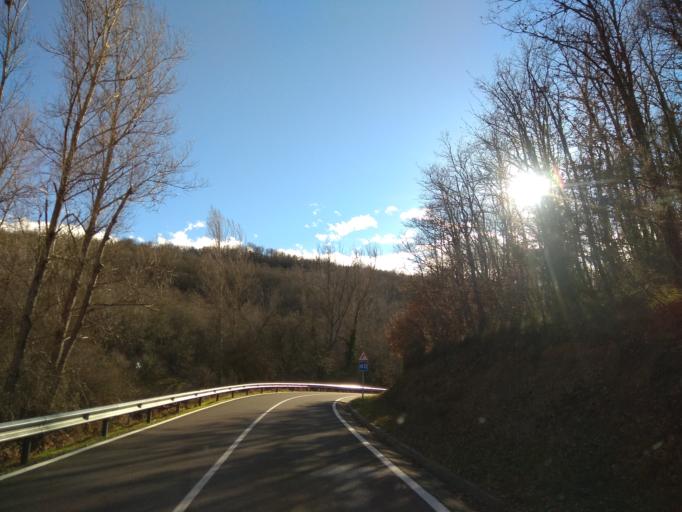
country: ES
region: Cantabria
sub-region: Provincia de Cantabria
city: San Martin de Elines
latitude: 42.8984
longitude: -3.8970
